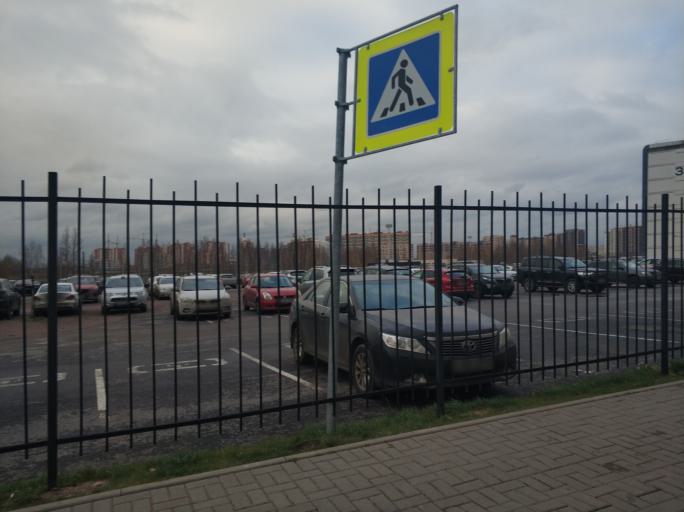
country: RU
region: Leningrad
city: Murino
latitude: 60.0535
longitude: 30.4472
